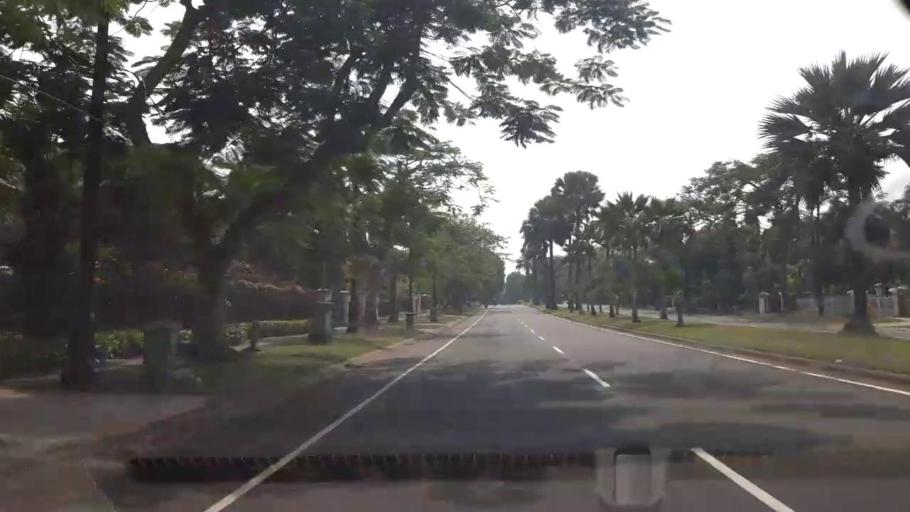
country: ID
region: Banten
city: Curug
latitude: -6.2406
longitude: 106.5986
